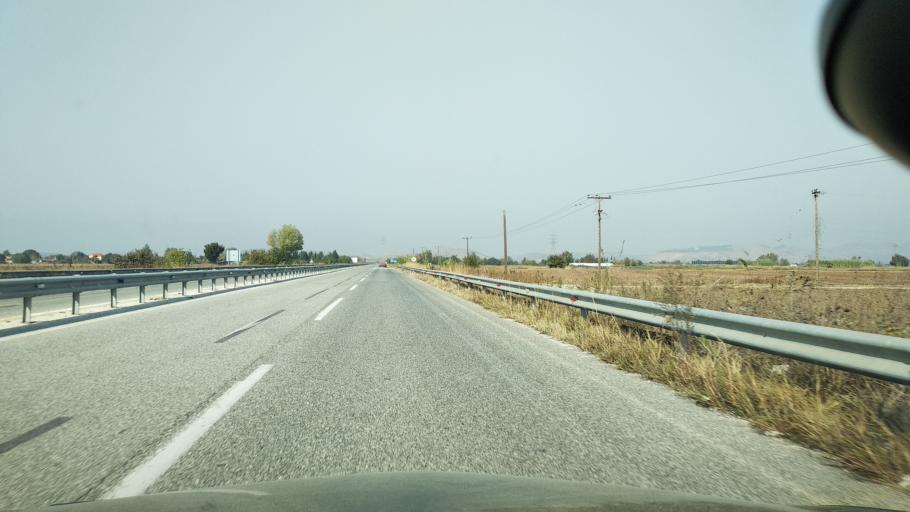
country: GR
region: Thessaly
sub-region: Trikala
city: Megalochori
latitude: 39.5631
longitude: 21.8549
